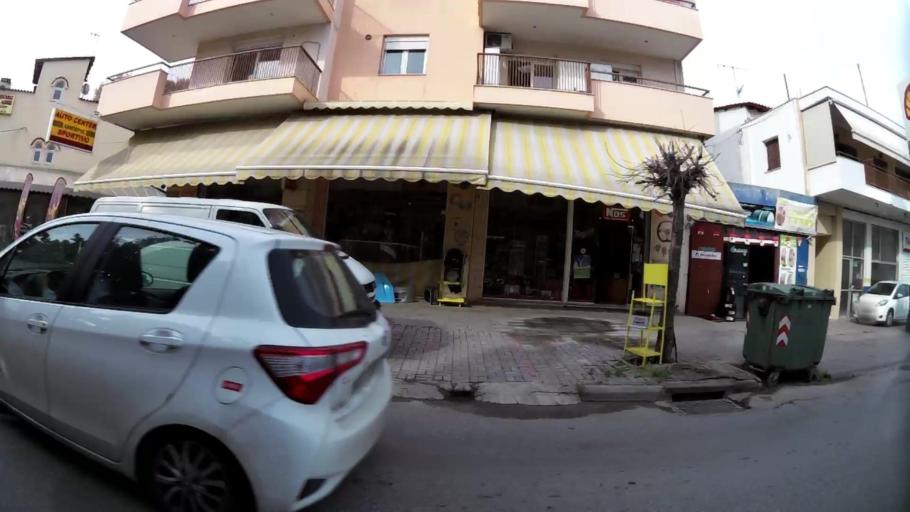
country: GR
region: Central Macedonia
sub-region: Nomos Thessalonikis
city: Thermi
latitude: 40.5520
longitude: 23.0187
